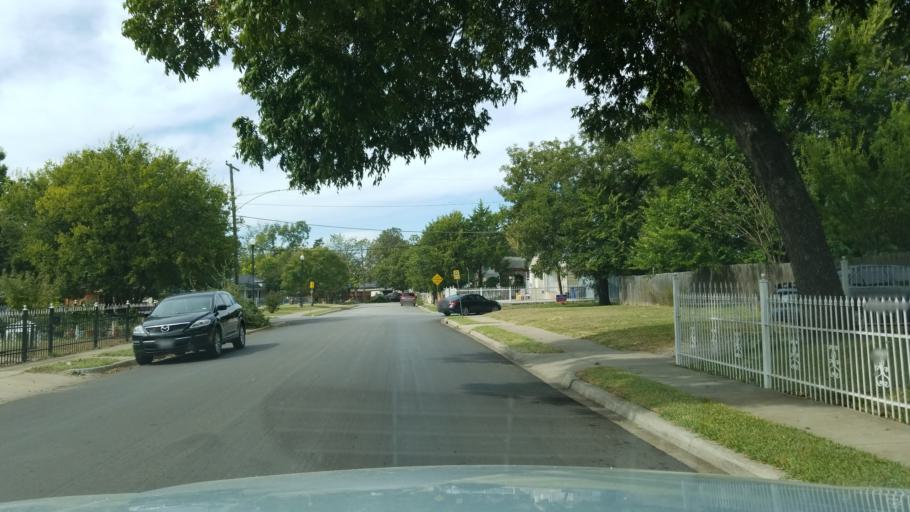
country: US
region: Texas
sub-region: Dallas County
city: Dallas
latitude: 32.7900
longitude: -96.7459
